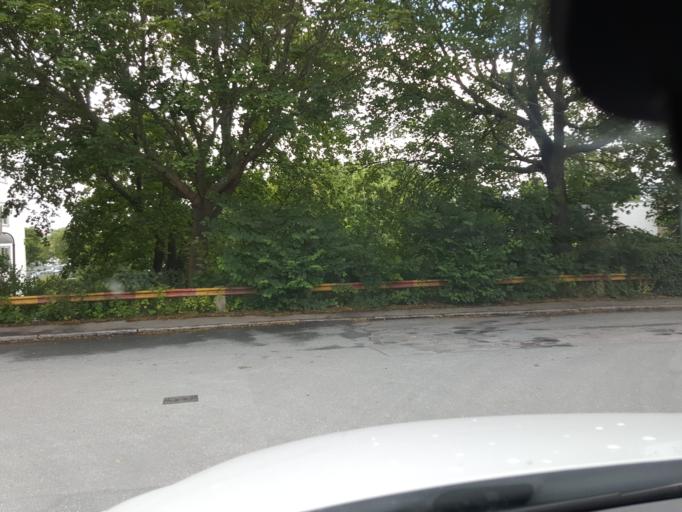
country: SE
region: Stockholm
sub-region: Stockholms Kommun
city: Bromma
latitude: 59.3206
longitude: 17.9724
